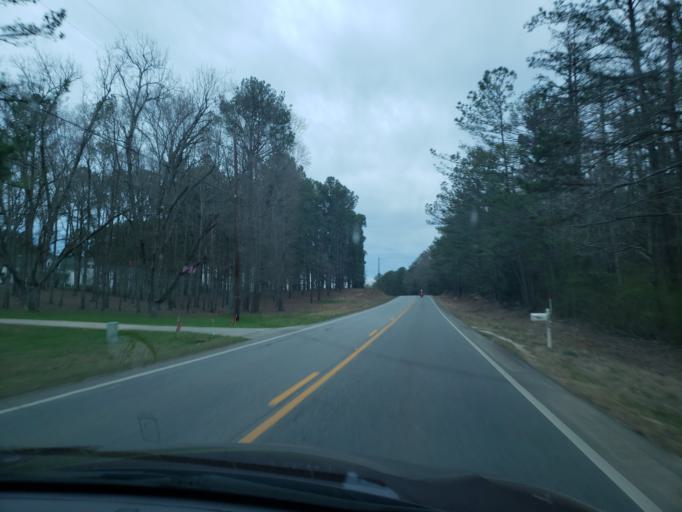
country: US
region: Alabama
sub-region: Chambers County
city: Lafayette
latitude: 32.9240
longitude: -85.3964
